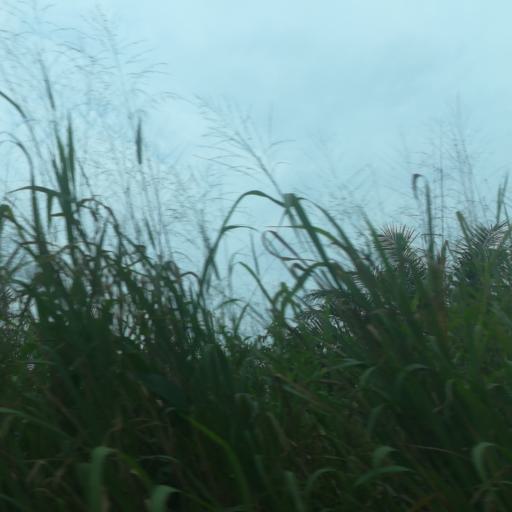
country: NG
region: Lagos
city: Ejirin
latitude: 6.6468
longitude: 3.7559
